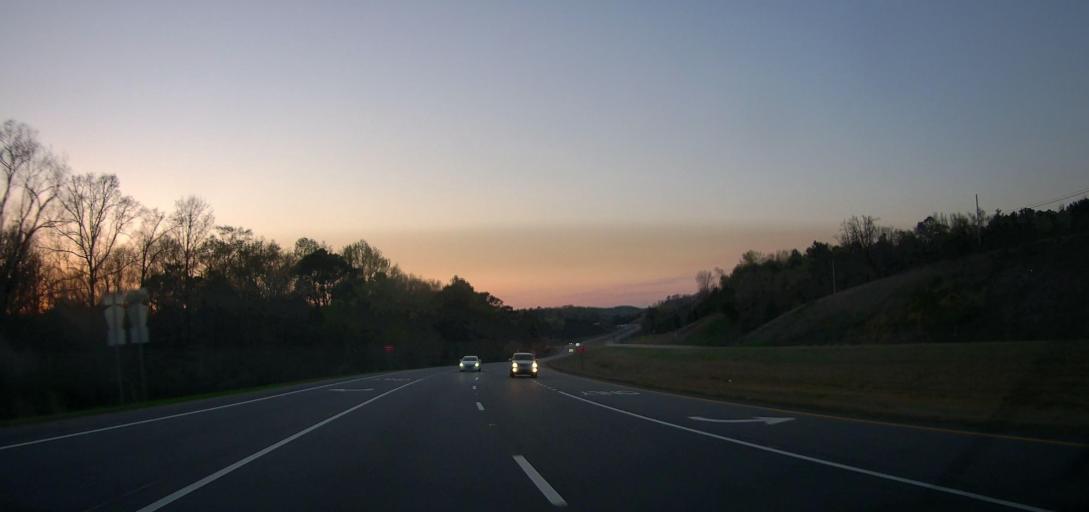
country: US
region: Alabama
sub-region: Tallapoosa County
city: Alexander City
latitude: 32.8868
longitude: -85.8722
